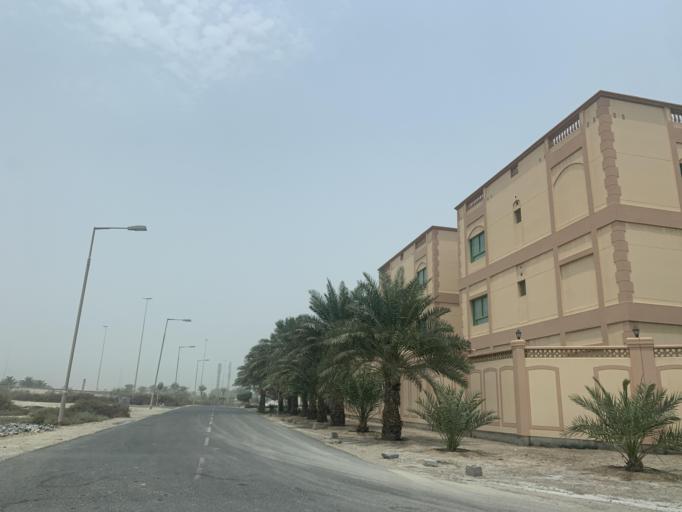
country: BH
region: Central Governorate
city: Madinat Hamad
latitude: 26.1697
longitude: 50.4677
